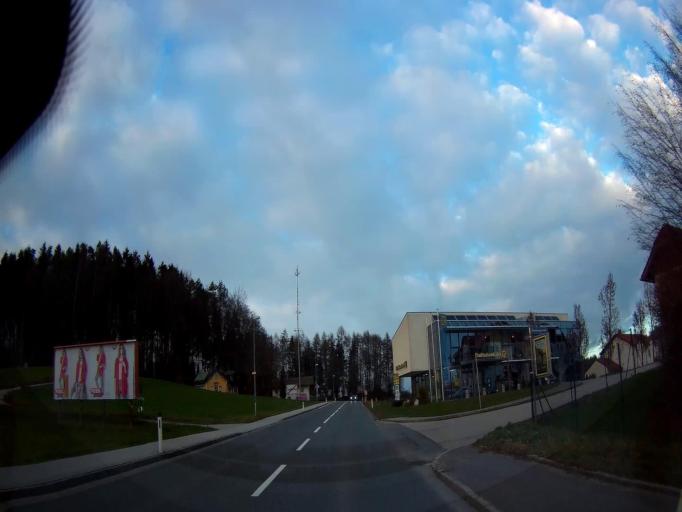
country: AT
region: Salzburg
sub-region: Politischer Bezirk Salzburg-Umgebung
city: Dorfbeuern
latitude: 48.0813
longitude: 12.9914
